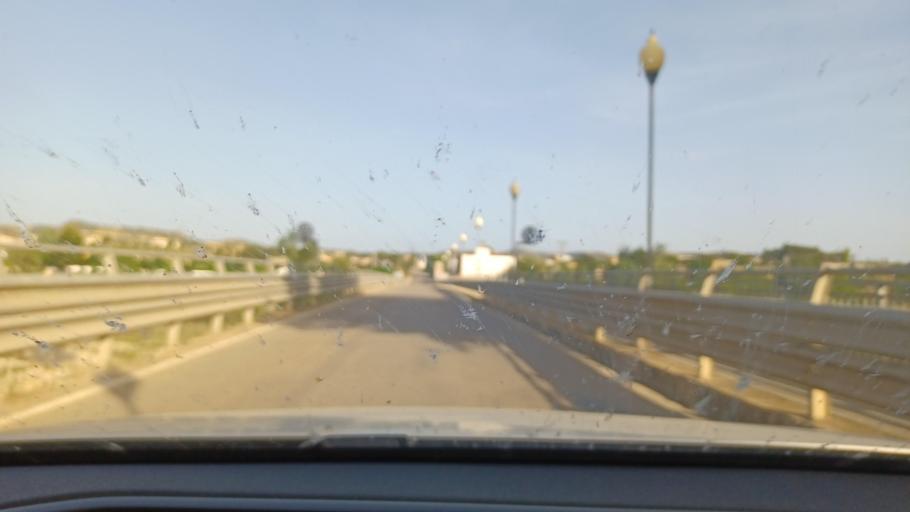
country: ES
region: Aragon
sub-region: Provincia de Zaragoza
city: Maella
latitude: 41.1200
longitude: 0.1413
